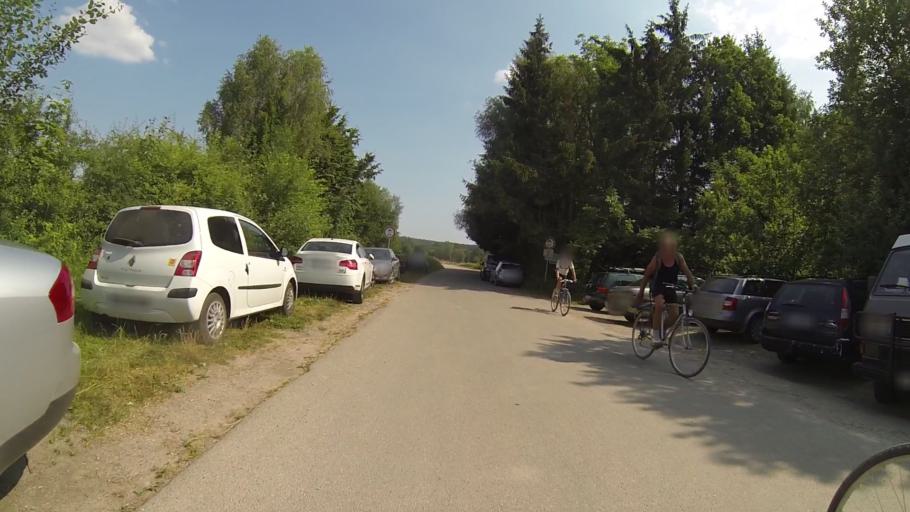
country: DE
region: Bavaria
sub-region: Swabia
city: Guenzburg
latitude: 48.4807
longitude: 10.3065
